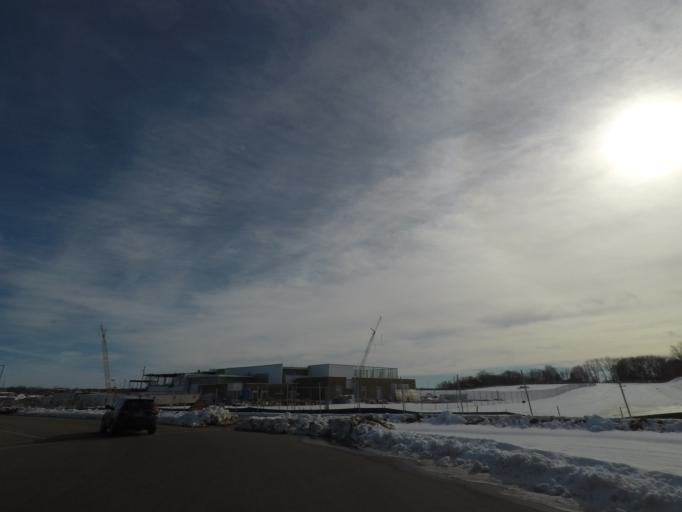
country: US
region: Wisconsin
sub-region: Dane County
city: Fitchburg
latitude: 43.0049
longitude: -89.4706
